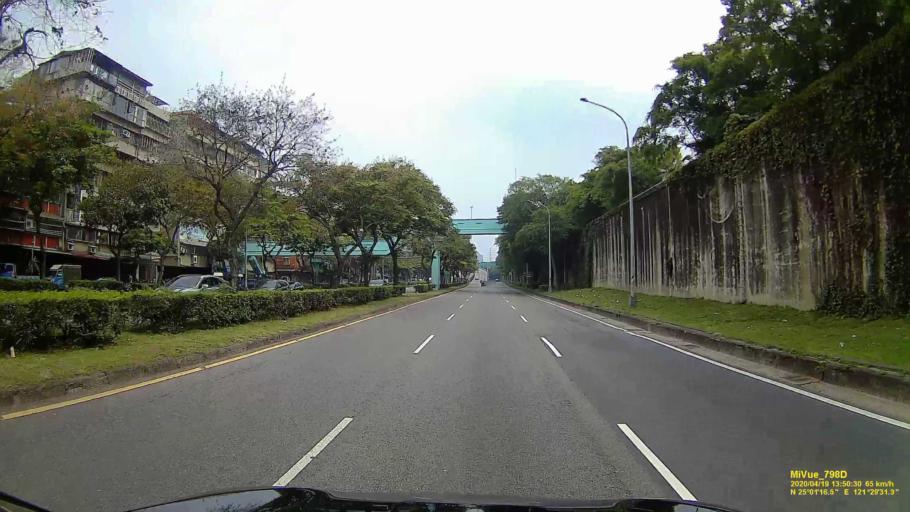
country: TW
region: Taipei
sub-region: Taipei
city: Banqiao
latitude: 25.0209
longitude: 121.4922
